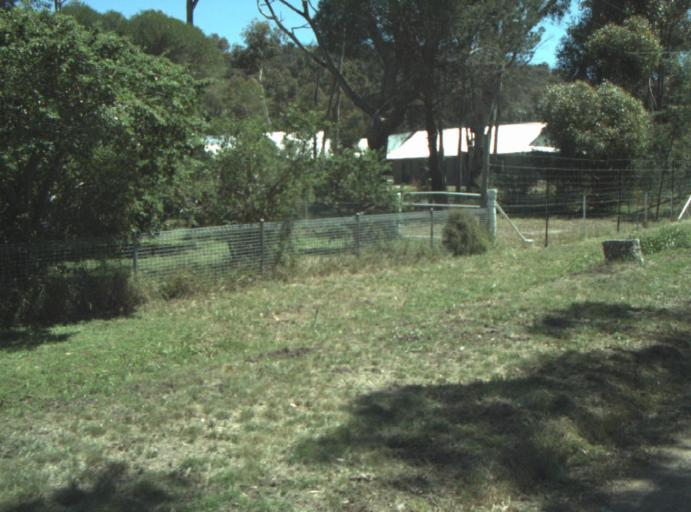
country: AU
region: Victoria
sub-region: Greater Geelong
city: Lara
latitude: -37.8447
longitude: 144.2826
